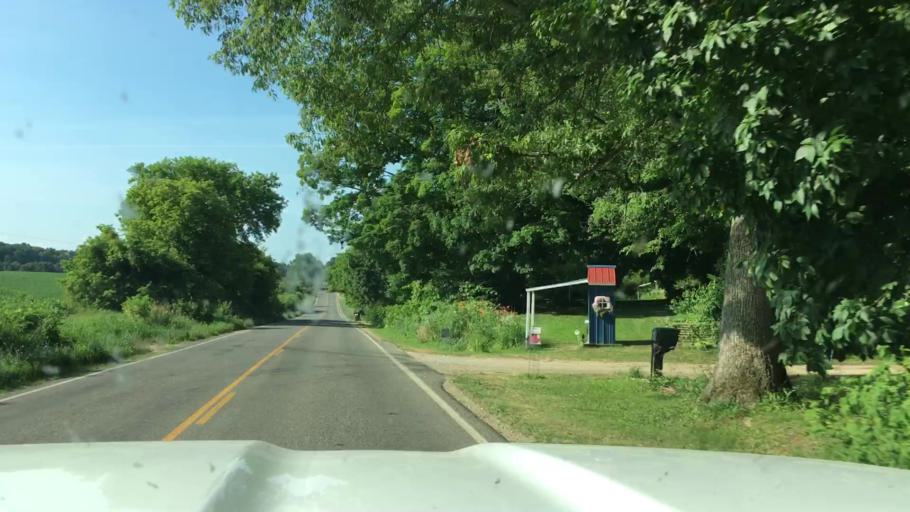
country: US
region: Michigan
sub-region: Barry County
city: Stony Point
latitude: 42.4463
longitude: -85.4544
